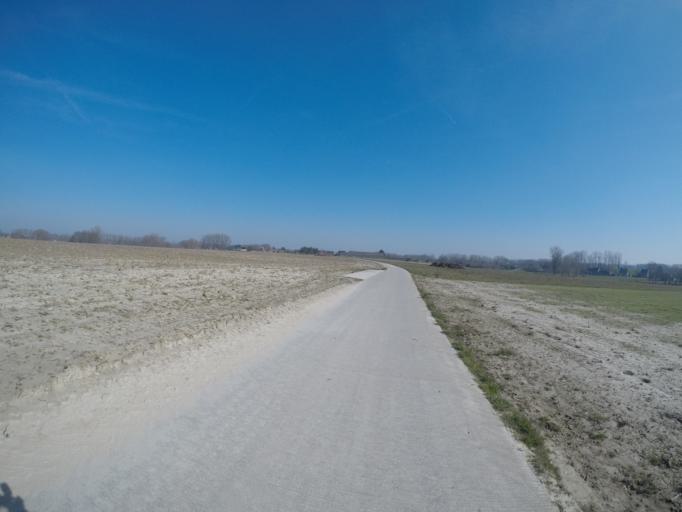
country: BE
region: Flanders
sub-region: Provincie Oost-Vlaanderen
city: Sint-Maria-Lierde
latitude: 50.7900
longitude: 3.8429
